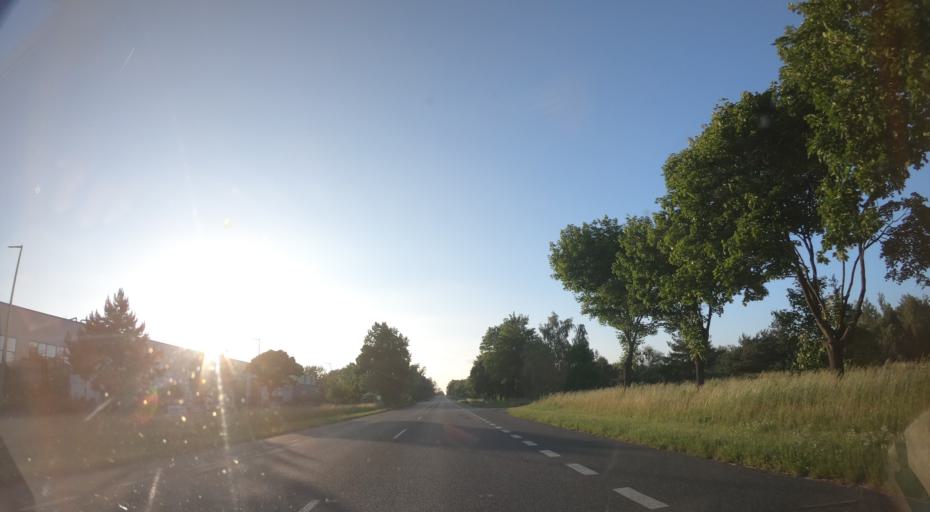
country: PL
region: West Pomeranian Voivodeship
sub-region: Powiat pyrzycki
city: Lipiany
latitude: 53.0167
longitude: 14.9365
